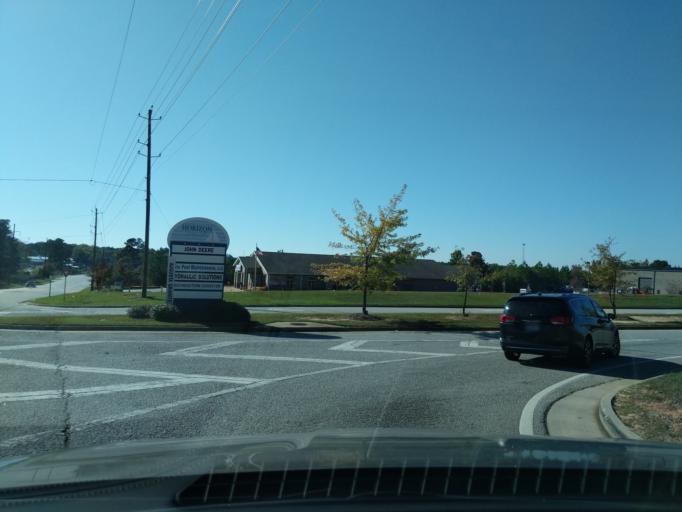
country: US
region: Georgia
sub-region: Columbia County
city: Grovetown
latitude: 33.4609
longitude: -82.1813
